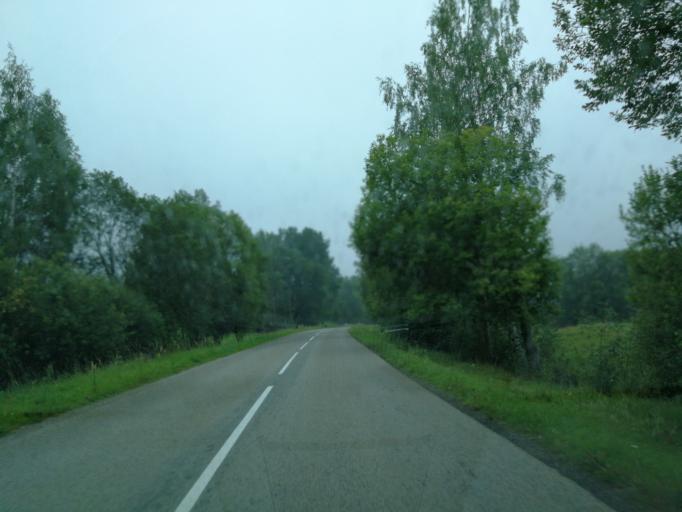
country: LV
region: Preilu Rajons
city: Jaunaglona
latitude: 56.2635
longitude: 27.0195
